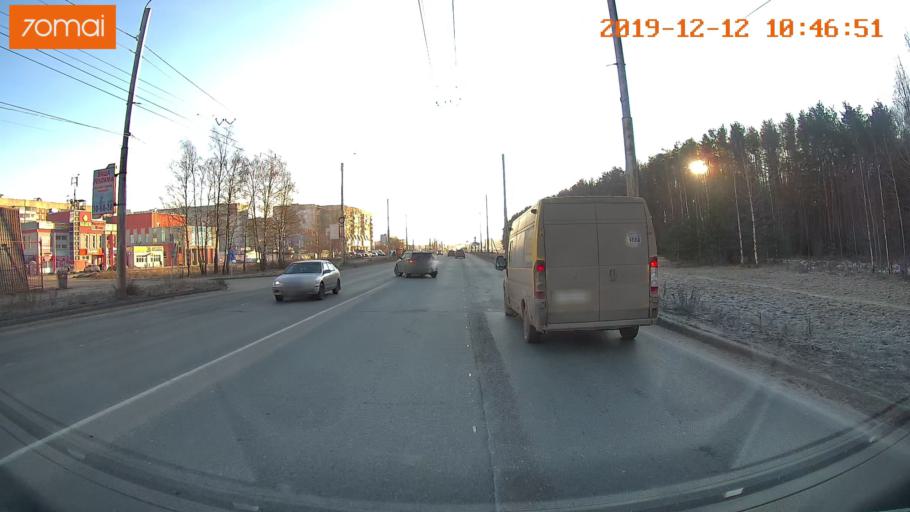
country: RU
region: Ivanovo
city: Kokhma
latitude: 56.9505
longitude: 41.0478
